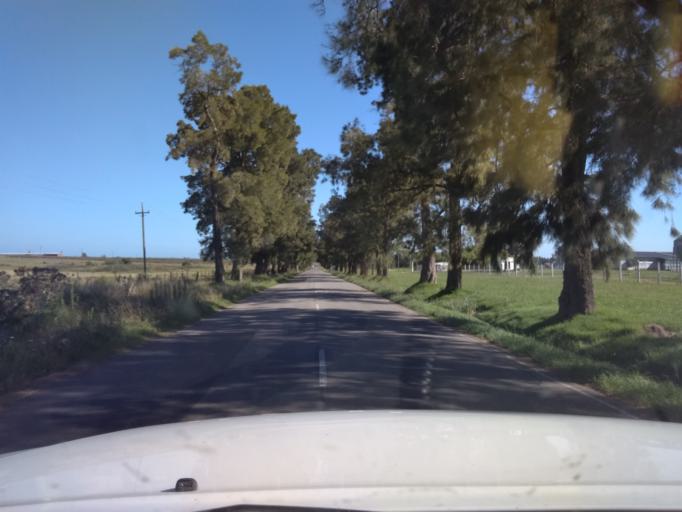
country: UY
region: Canelones
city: San Bautista
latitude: -34.3920
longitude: -55.9596
